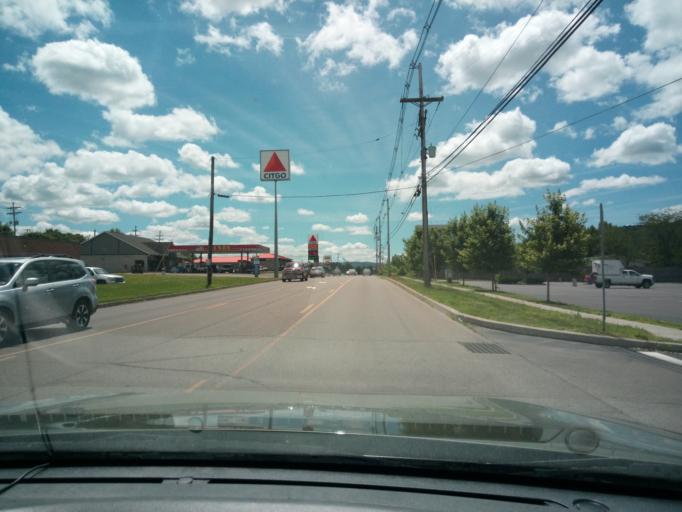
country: US
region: Pennsylvania
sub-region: Bradford County
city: South Waverly
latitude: 41.9875
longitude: -76.5461
